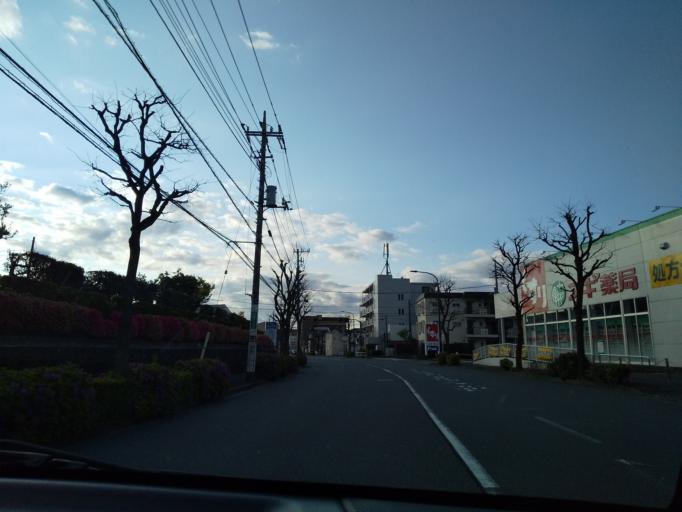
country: JP
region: Tokyo
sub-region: Machida-shi
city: Machida
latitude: 35.5527
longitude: 139.4291
